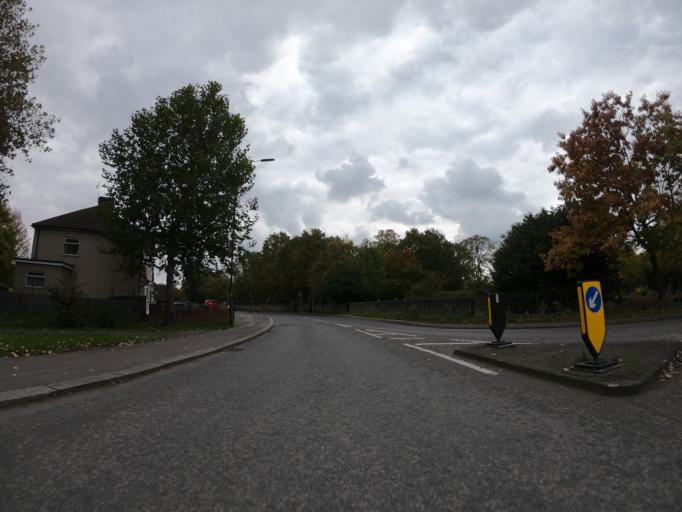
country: GB
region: England
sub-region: Greater London
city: Erith
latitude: 51.4884
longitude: 0.1685
